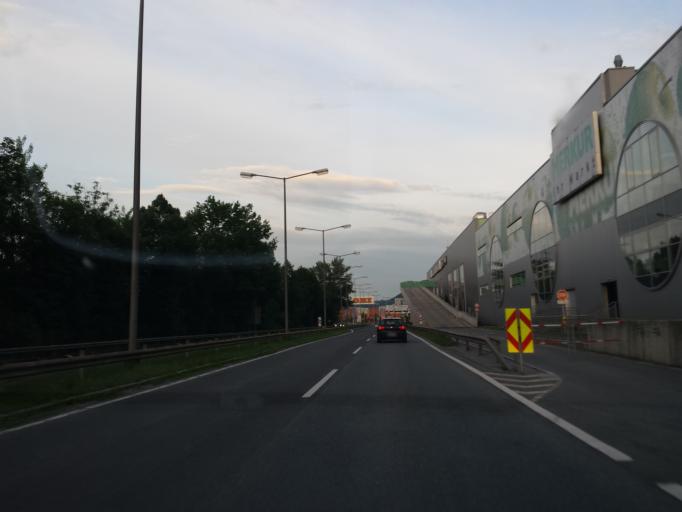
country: AT
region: Styria
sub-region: Graz Stadt
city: Goesting
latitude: 47.1059
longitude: 15.3966
